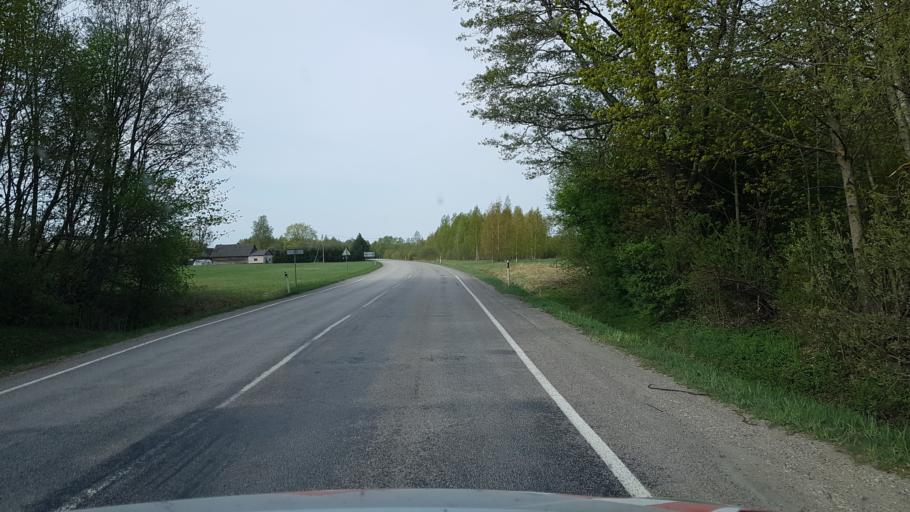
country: EE
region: Paernumaa
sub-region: Audru vald
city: Audru
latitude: 58.4047
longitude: 24.3042
